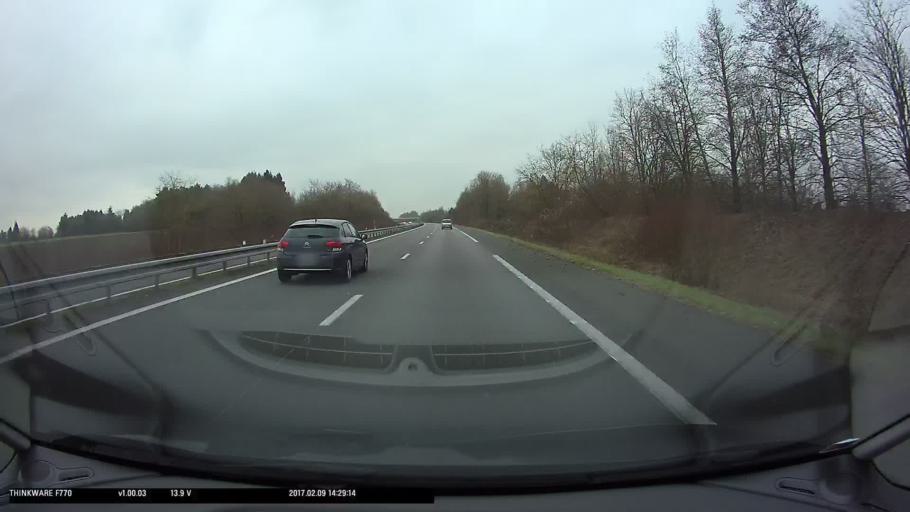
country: FR
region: Centre
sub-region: Departement du Cher
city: Mehun-sur-Yevre
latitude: 47.1168
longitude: 2.1972
